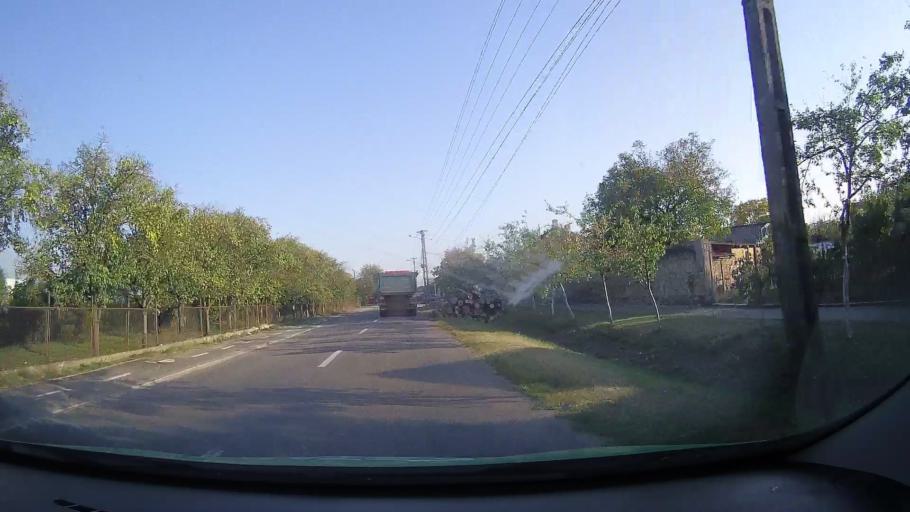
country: RO
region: Arad
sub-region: Comuna Pancota
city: Pancota
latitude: 46.3199
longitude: 21.6933
